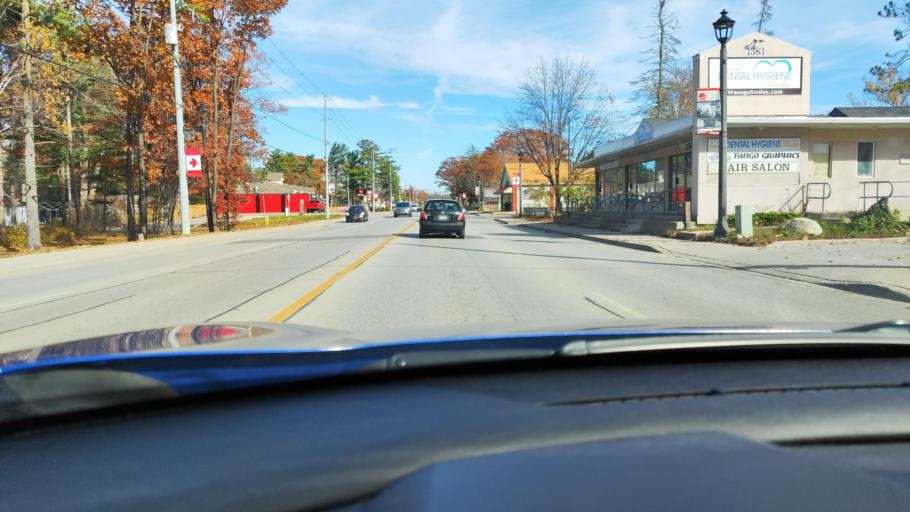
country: CA
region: Ontario
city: Wasaga Beach
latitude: 44.4864
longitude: -80.0557
